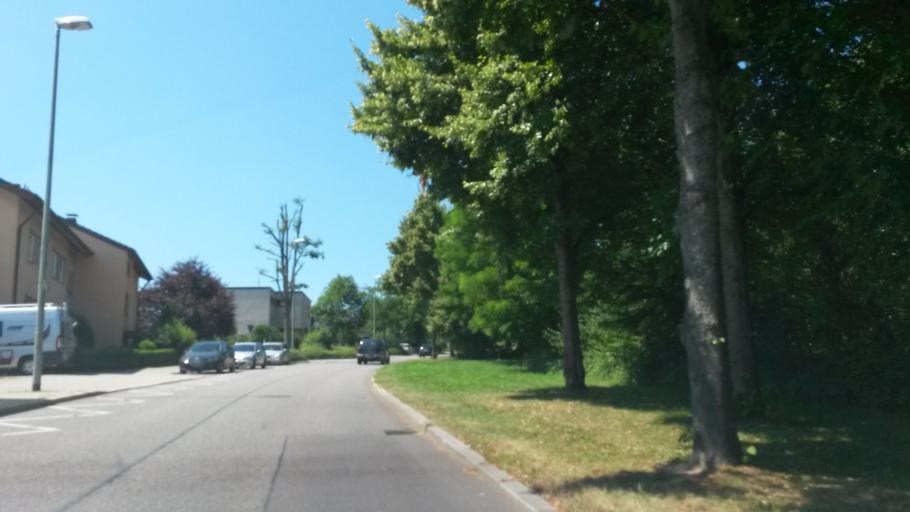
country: DE
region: Baden-Wuerttemberg
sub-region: Karlsruhe Region
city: Birkenfeld
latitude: 48.8843
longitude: 8.6485
